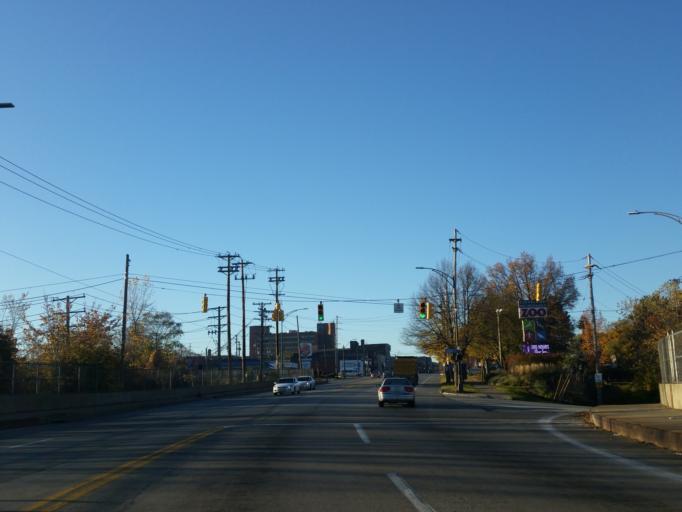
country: US
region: Ohio
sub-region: Cuyahoga County
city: Brooklyn Heights
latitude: 41.4446
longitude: -81.7032
